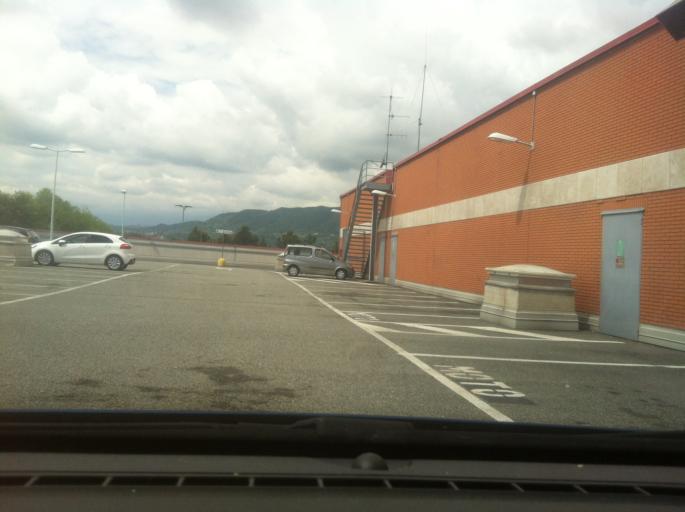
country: IT
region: Piedmont
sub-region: Provincia di Torino
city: Pavone Canavese
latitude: 45.4447
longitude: 7.8538
